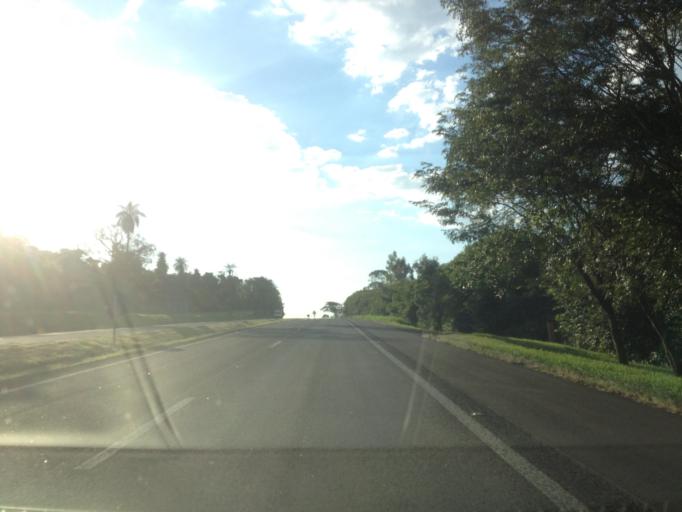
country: BR
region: Sao Paulo
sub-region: Brotas
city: Brotas
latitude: -22.2530
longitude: -48.2469
